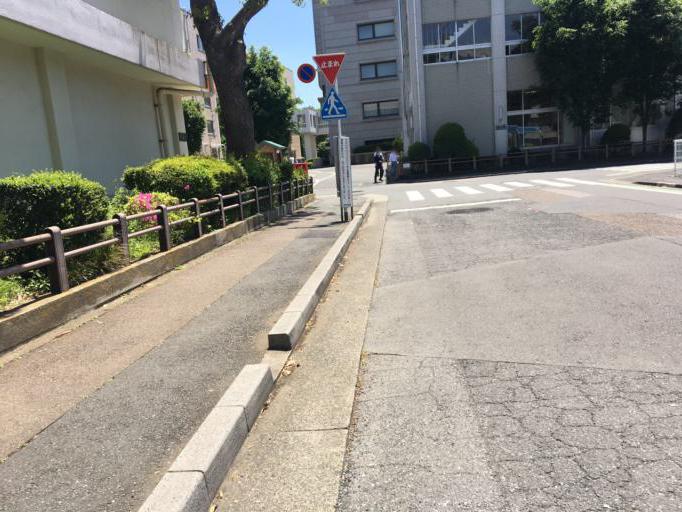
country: JP
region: Saitama
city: Yono
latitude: 35.8582
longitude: 139.6481
